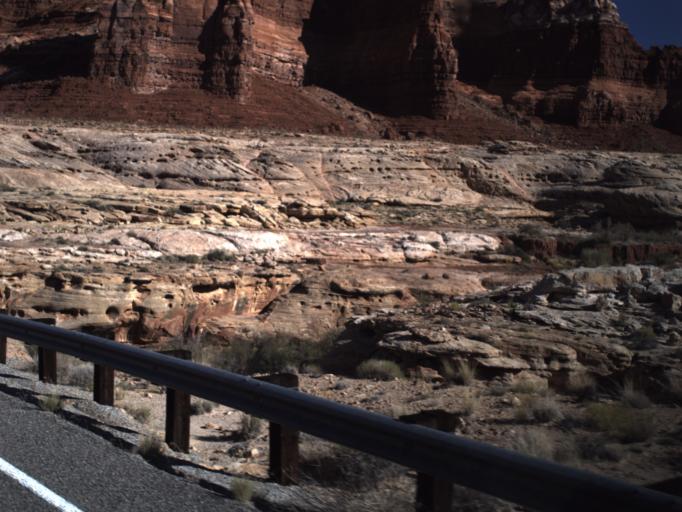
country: US
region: Utah
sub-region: San Juan County
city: Blanding
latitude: 37.9034
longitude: -110.3791
